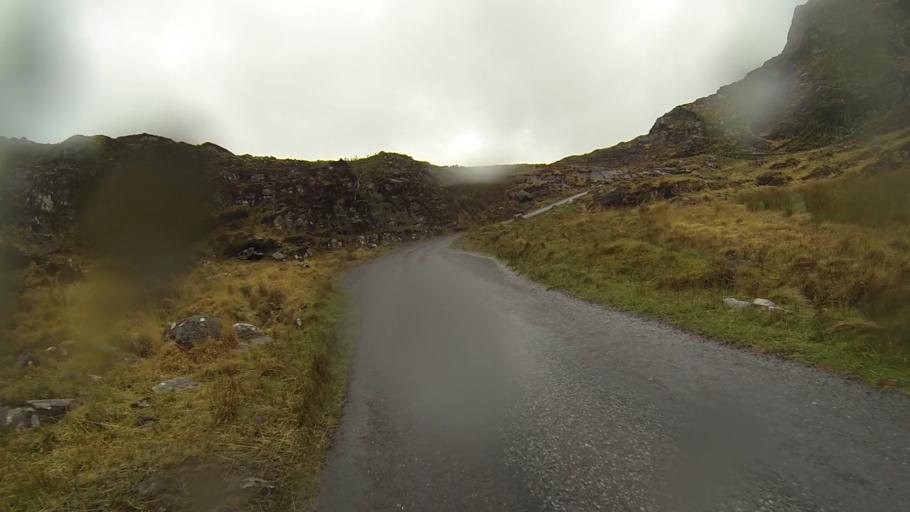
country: IE
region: Munster
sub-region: Ciarrai
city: Kenmare
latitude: 51.9960
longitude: -9.6441
